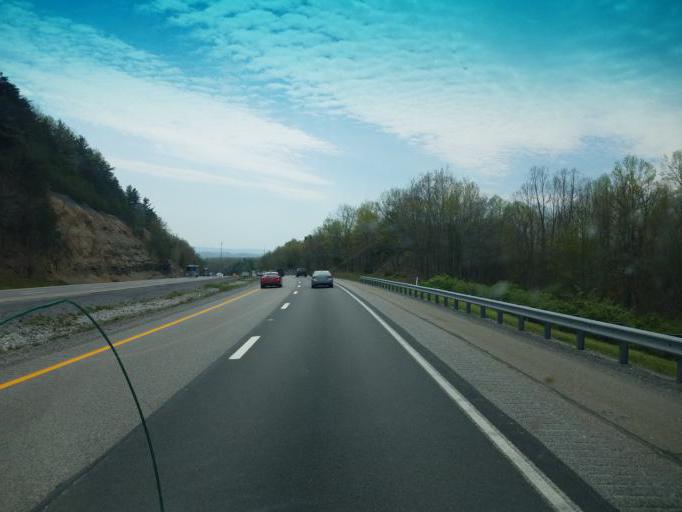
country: US
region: West Virginia
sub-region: Mercer County
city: Athens
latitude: 37.5425
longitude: -81.1161
